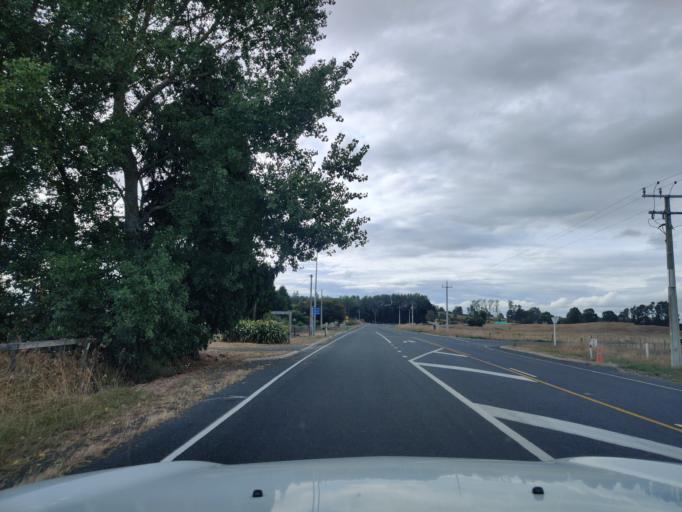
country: NZ
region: Waikato
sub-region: Waipa District
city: Cambridge
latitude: -37.8095
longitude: 175.4513
